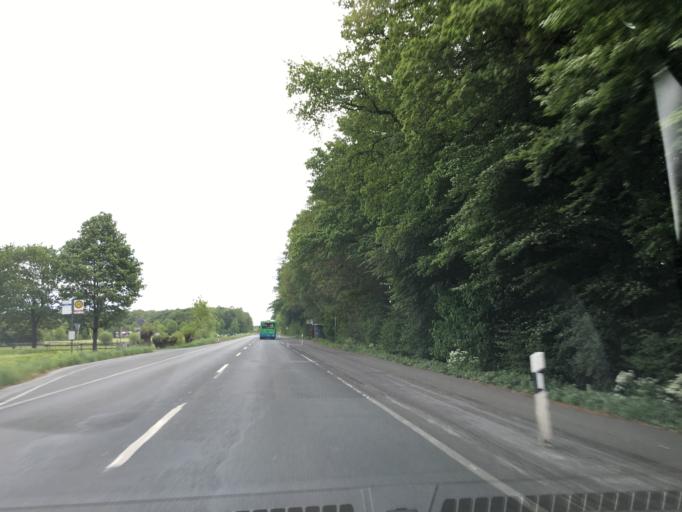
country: DE
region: North Rhine-Westphalia
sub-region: Regierungsbezirk Munster
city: Senden
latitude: 51.9245
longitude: 7.5349
